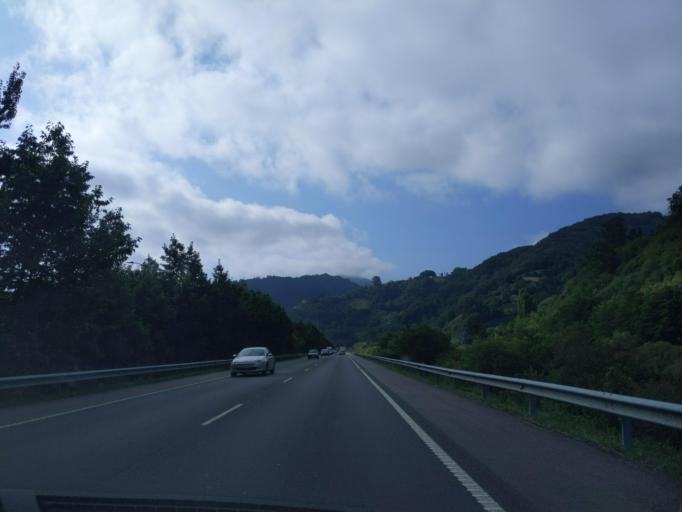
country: ES
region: Asturias
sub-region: Province of Asturias
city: El entrego
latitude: 43.2803
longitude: -5.6183
